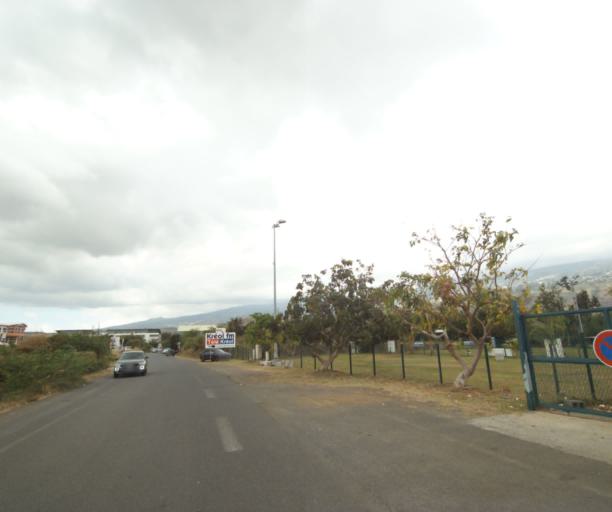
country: RE
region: Reunion
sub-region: Reunion
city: Saint-Paul
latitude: -20.9886
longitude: 55.2945
